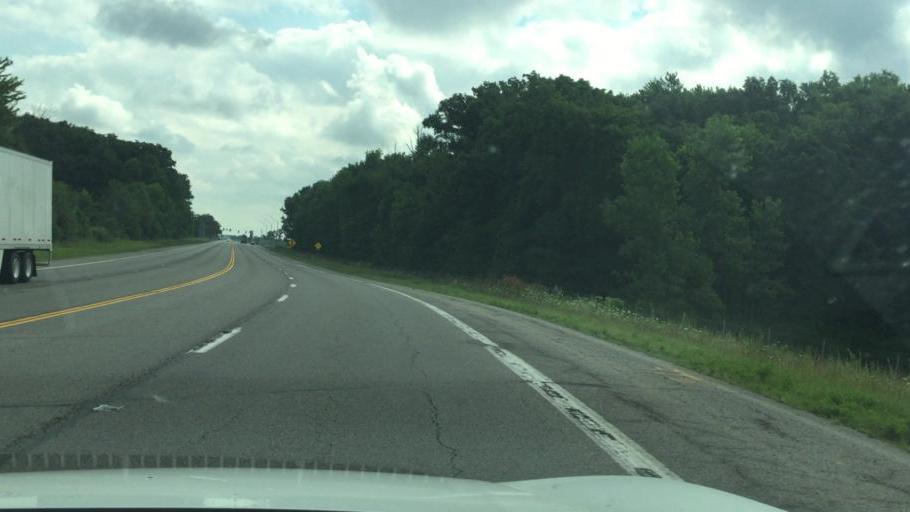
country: US
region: Ohio
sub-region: Champaign County
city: North Lewisburg
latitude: 40.3302
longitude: -83.5644
